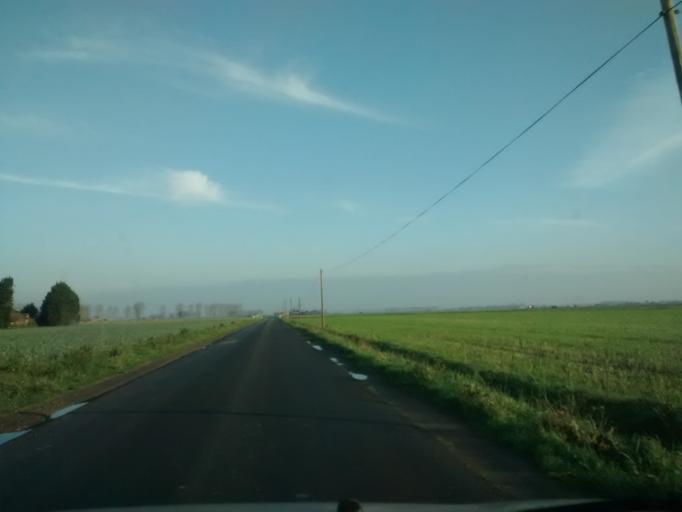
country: FR
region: Brittany
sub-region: Departement d'Ille-et-Vilaine
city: Roz-sur-Couesnon
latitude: 48.5887
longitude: -1.5434
